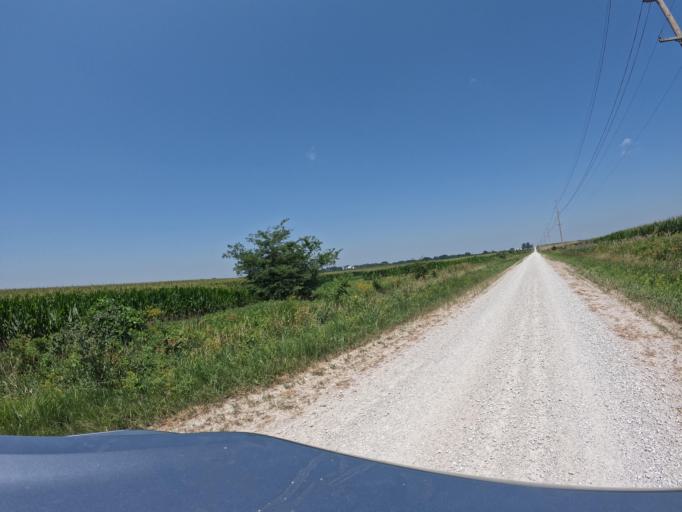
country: US
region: Iowa
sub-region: Keokuk County
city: Sigourney
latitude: 41.2911
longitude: -92.1807
